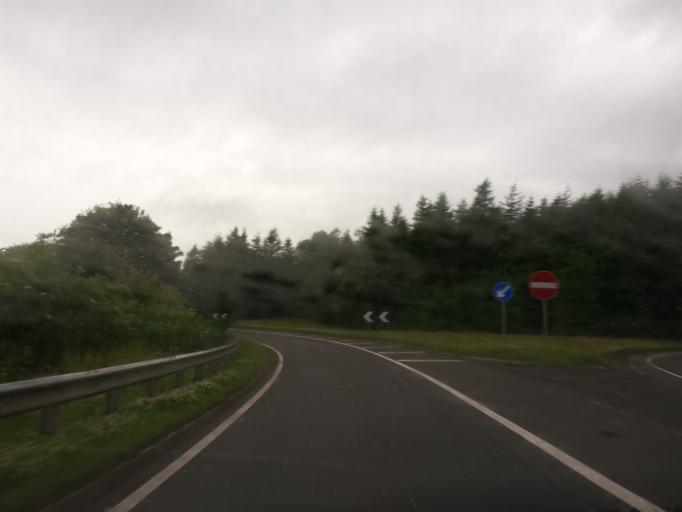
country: GB
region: Scotland
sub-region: Perth and Kinross
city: Luncarty
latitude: 56.4088
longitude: -3.4799
